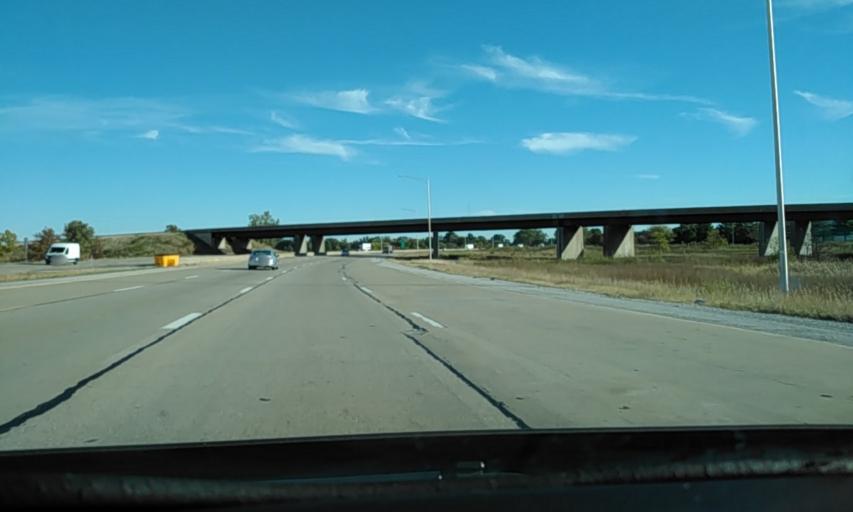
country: US
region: Illinois
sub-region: Saint Clair County
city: Dupo
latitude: 38.5285
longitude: -90.1974
